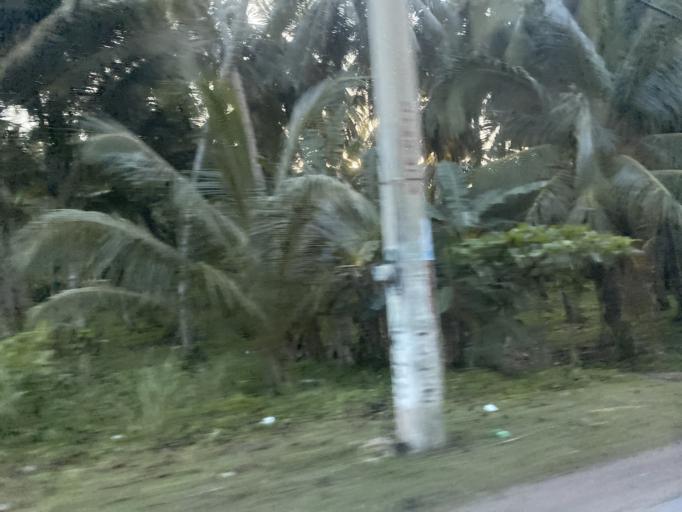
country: DO
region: Maria Trinidad Sanchez
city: Nagua
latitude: 19.3630
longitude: -69.8339
